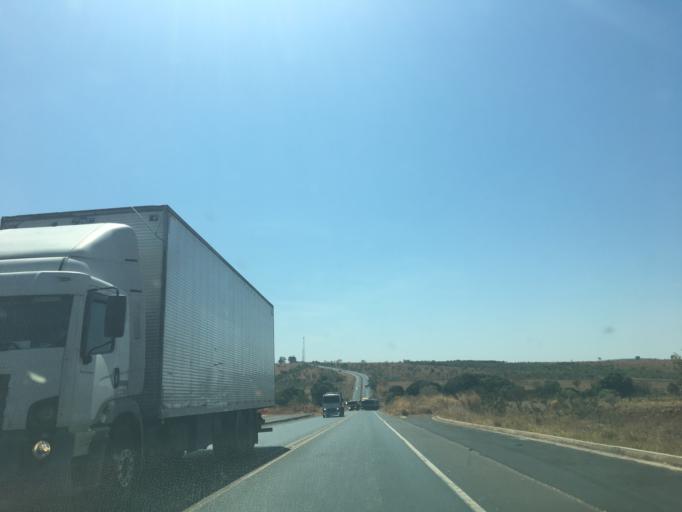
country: BR
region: Minas Gerais
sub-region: Monte Alegre De Minas
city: Monte Alegre de Minas
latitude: -18.8833
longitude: -49.0537
